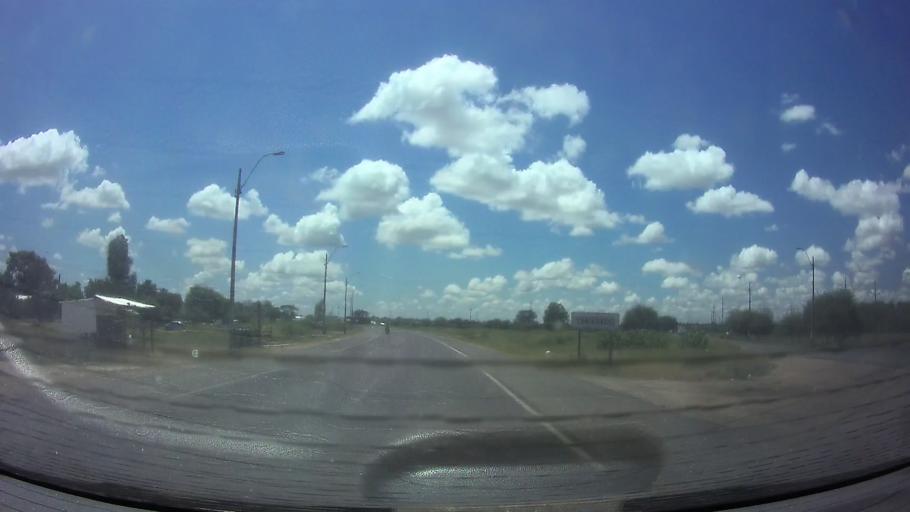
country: PY
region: Central
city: Colonia Mariano Roque Alonso
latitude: -25.1716
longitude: -57.5669
